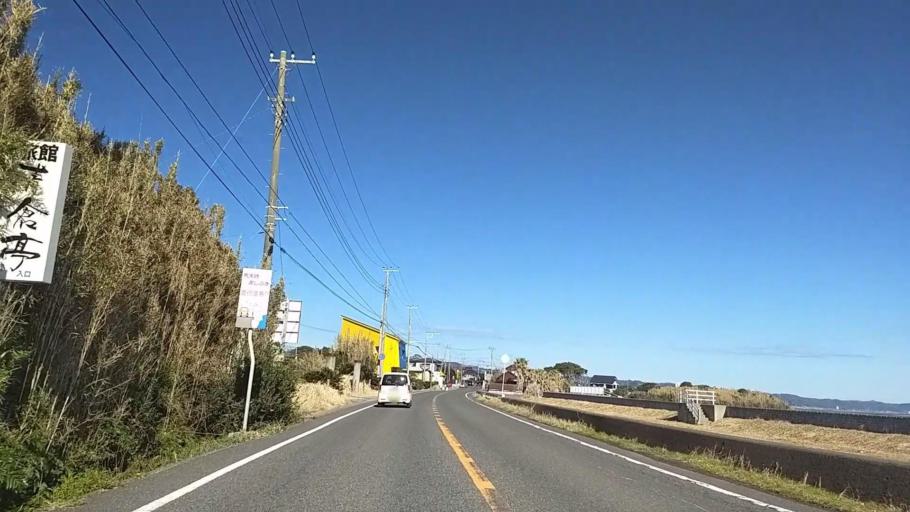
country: JP
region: Chiba
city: Tateyama
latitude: 34.9802
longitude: 139.9666
